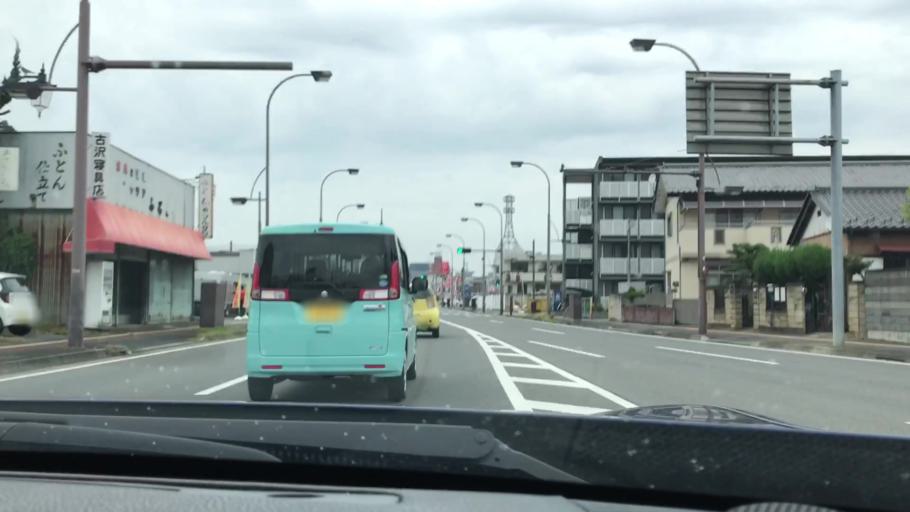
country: JP
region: Gunma
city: Maebashi-shi
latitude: 36.3766
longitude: 139.0702
